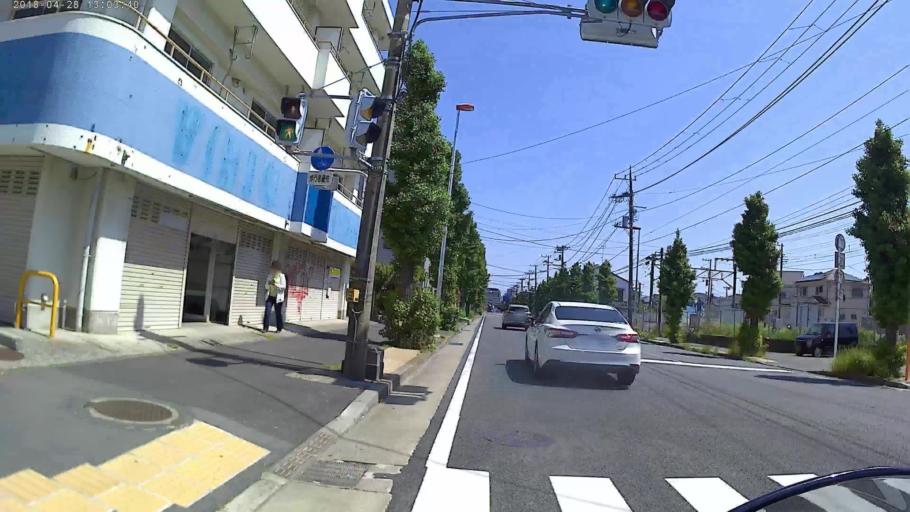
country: JP
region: Kanagawa
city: Yokosuka
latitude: 35.2508
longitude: 139.6793
